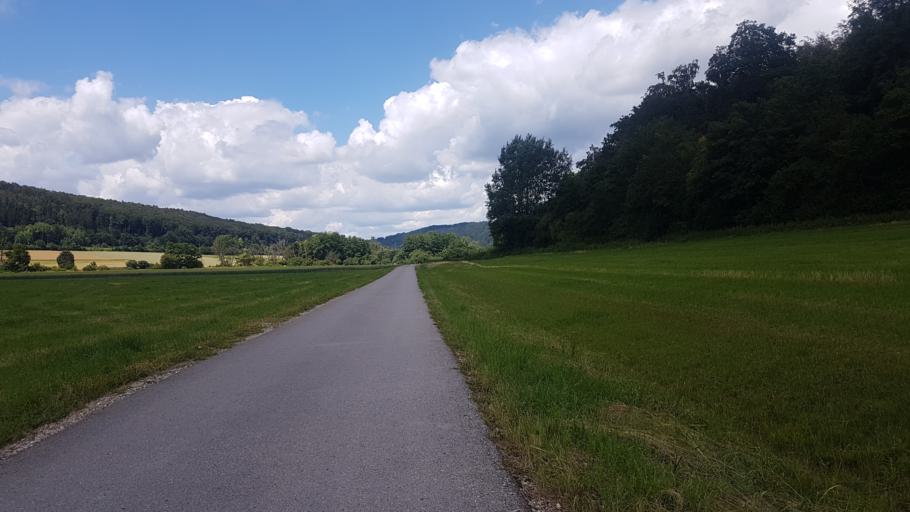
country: DE
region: Bavaria
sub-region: Upper Bavaria
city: Eichstaett
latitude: 48.8829
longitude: 11.1479
